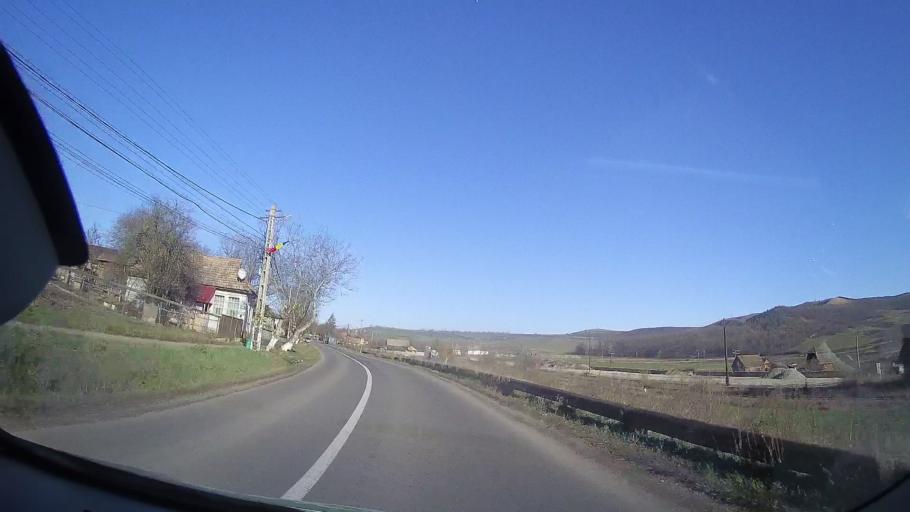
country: RO
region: Mures
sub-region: Comuna Sarmasu
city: Balda
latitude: 46.7307
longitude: 24.1458
